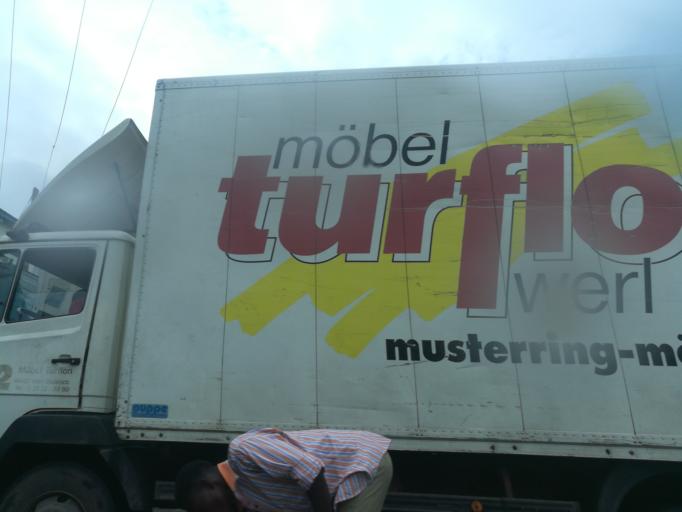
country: NG
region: Lagos
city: Agege
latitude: 6.6242
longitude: 3.3365
